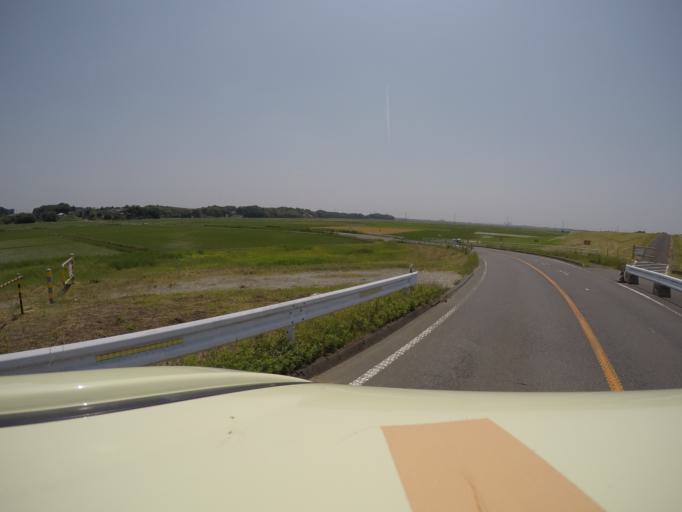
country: JP
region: Ibaraki
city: Iwai
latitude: 35.9896
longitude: 139.9238
